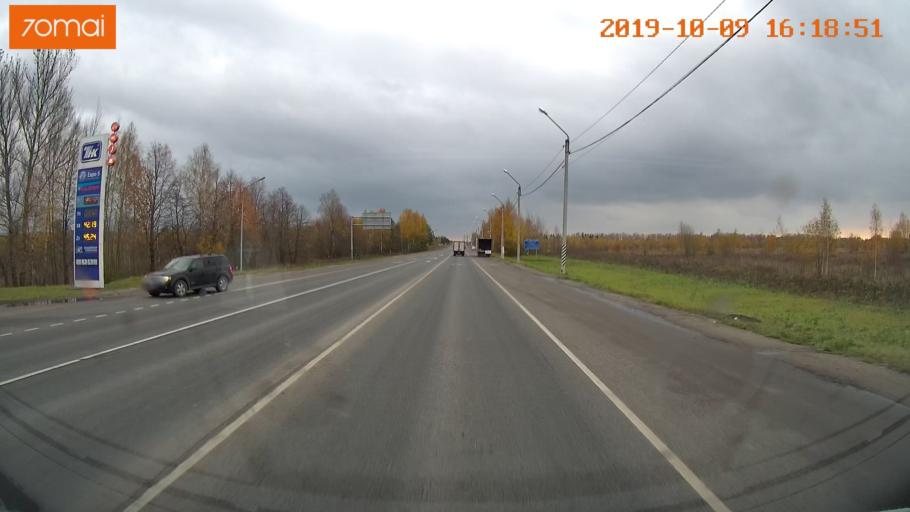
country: RU
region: Kostroma
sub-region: Kostromskoy Rayon
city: Kostroma
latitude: 57.7250
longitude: 40.8960
